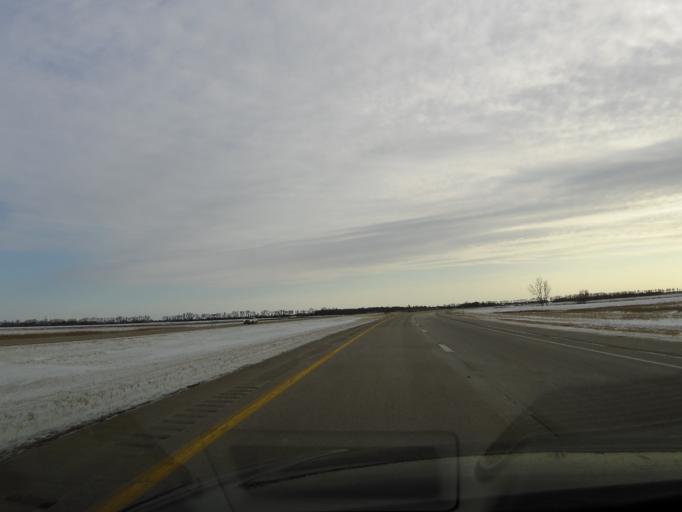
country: US
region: North Dakota
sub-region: Walsh County
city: Grafton
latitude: 48.4705
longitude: -97.1906
